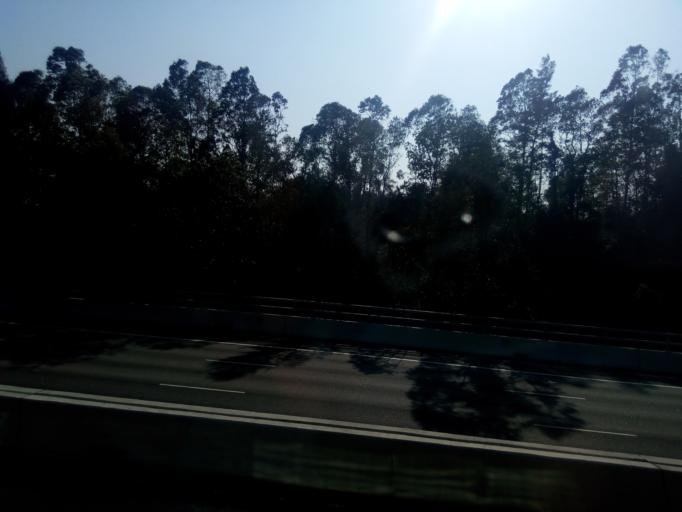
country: HK
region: Tsuen Wan
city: Tsuen Wan
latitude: 22.3703
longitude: 114.0756
